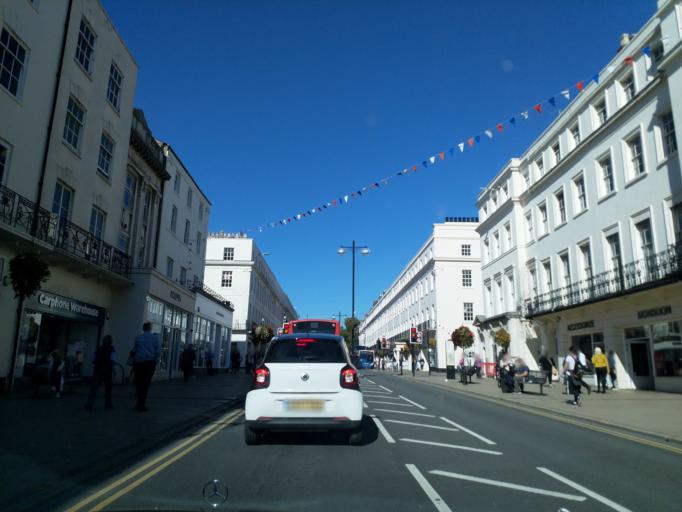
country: GB
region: England
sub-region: Warwickshire
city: Royal Leamington Spa
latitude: 52.2915
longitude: -1.5357
